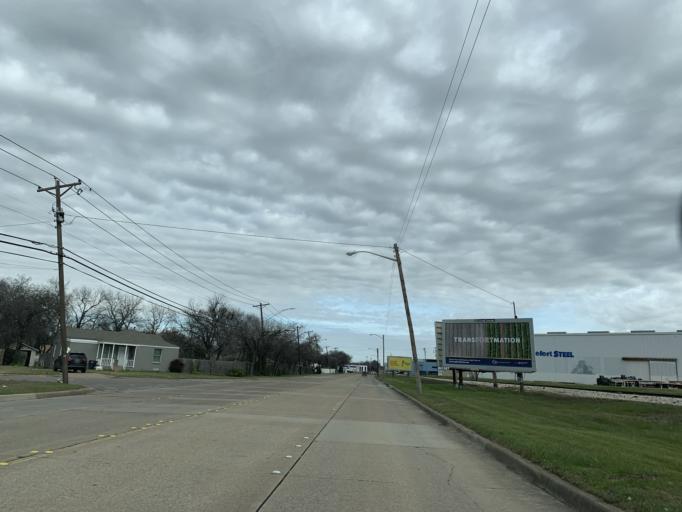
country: US
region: Texas
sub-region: Tarrant County
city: Edgecliff Village
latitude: 32.6987
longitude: -97.3561
